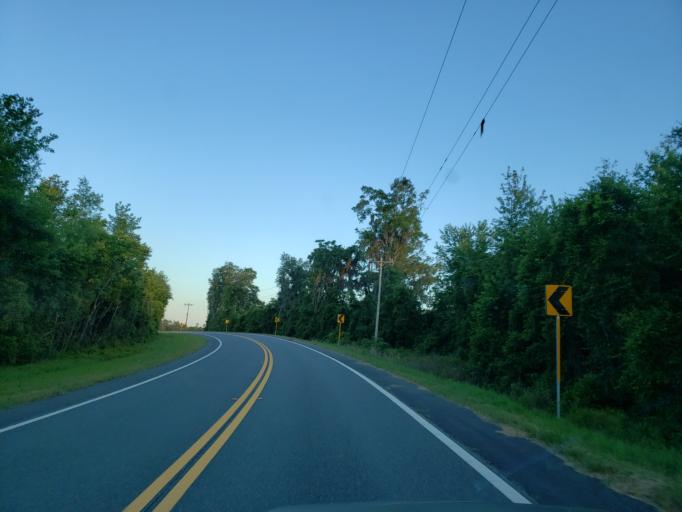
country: US
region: Florida
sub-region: Madison County
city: Madison
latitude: 30.5819
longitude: -83.2402
